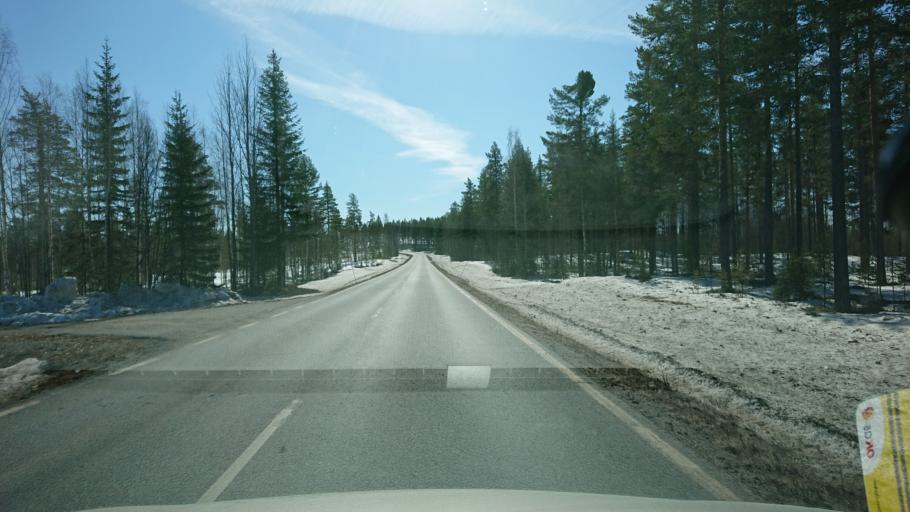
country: SE
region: Vaesterbotten
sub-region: Dorotea Kommun
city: Dorotea
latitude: 64.0285
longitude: 16.2731
